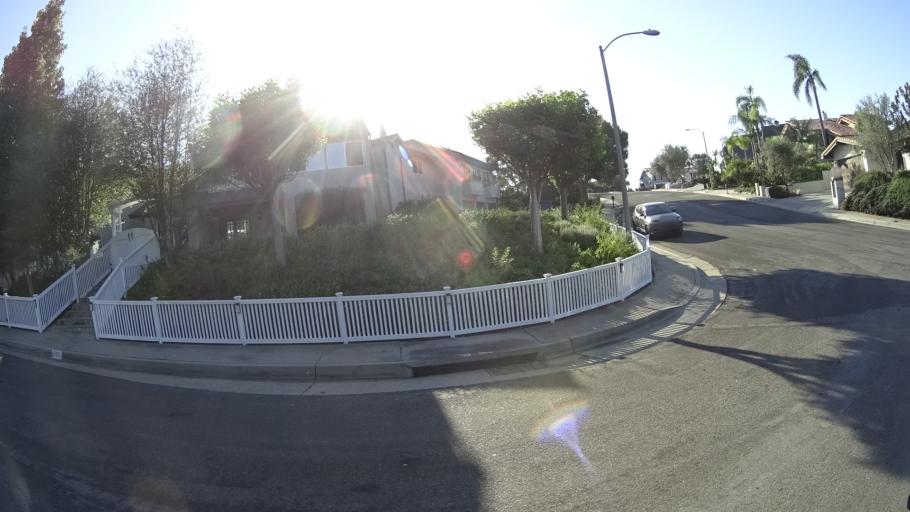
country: US
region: California
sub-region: Orange County
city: San Clemente
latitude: 33.4178
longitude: -117.5893
